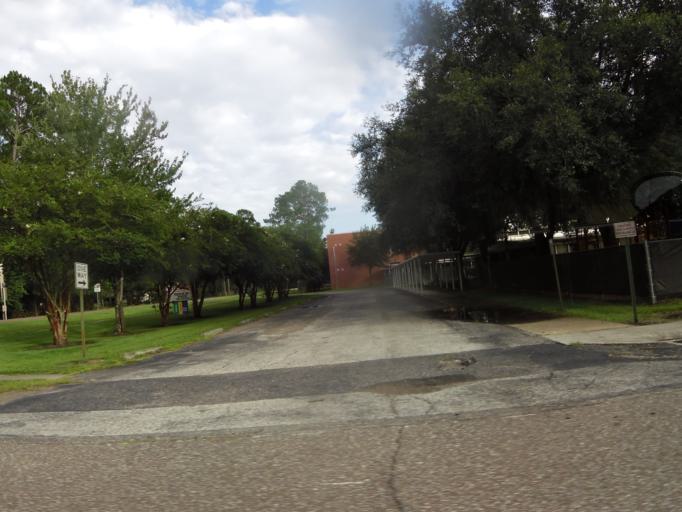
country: US
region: Florida
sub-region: Nassau County
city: Nassau Village-Ratliff
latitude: 30.4265
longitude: -81.7661
